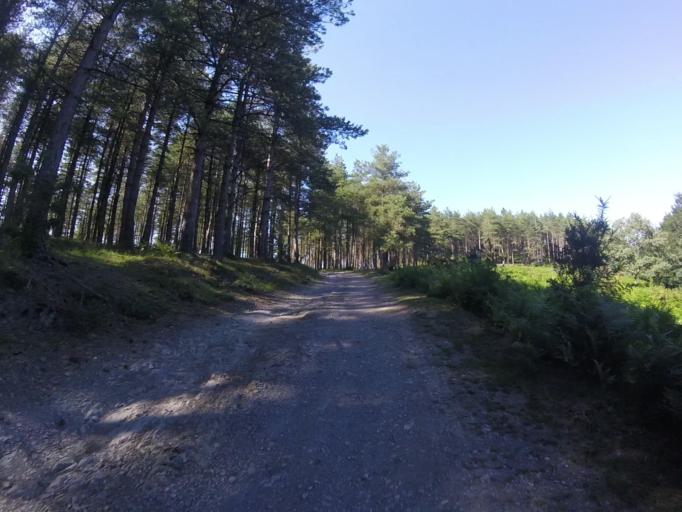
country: ES
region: Basque Country
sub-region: Provincia de Guipuzcoa
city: Irun
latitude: 43.2969
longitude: -1.7852
